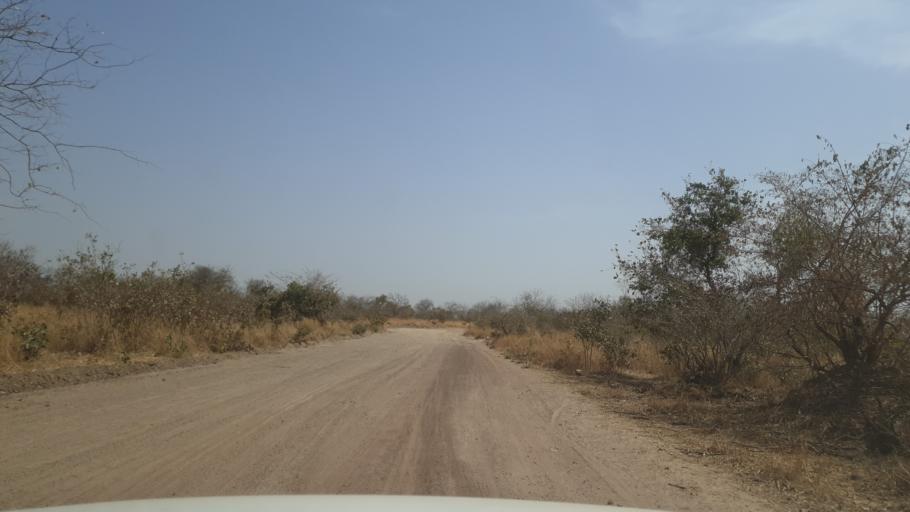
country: ML
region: Koulikoro
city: Kolokani
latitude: 13.5090
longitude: -8.1703
